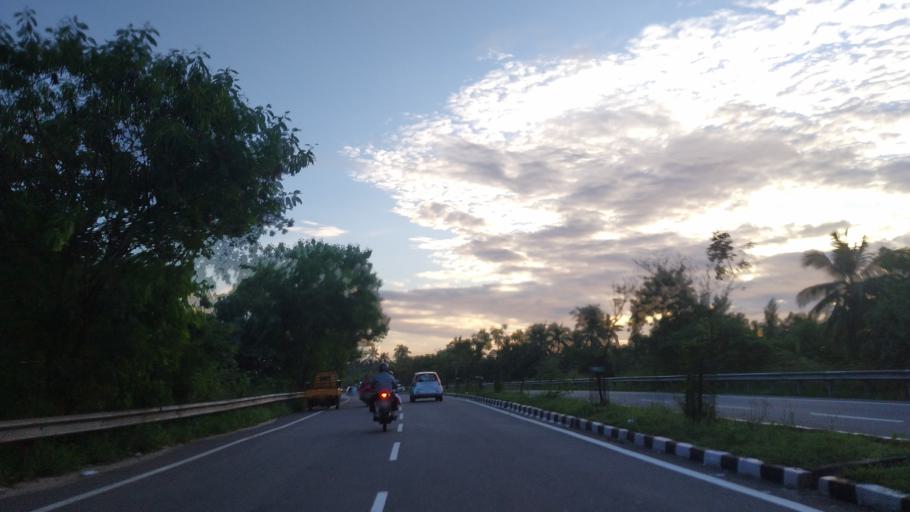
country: IN
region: Kerala
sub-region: Ernakulam
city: Elur
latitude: 10.0600
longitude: 76.2863
